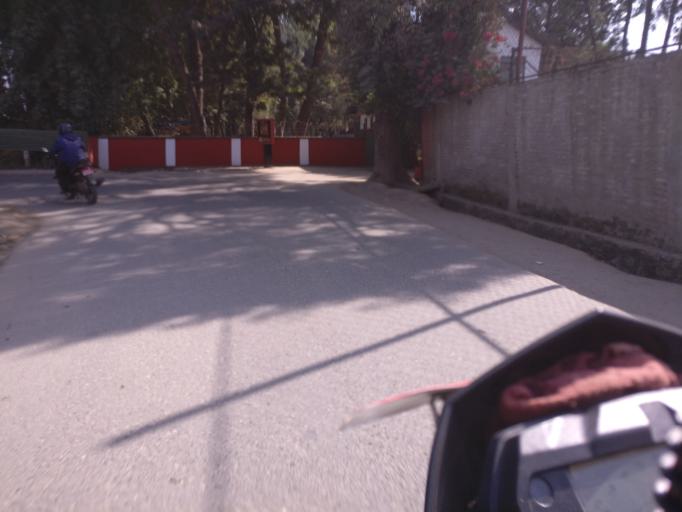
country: NP
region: Central Region
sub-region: Bagmati Zone
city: Patan
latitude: 27.6652
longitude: 85.3214
